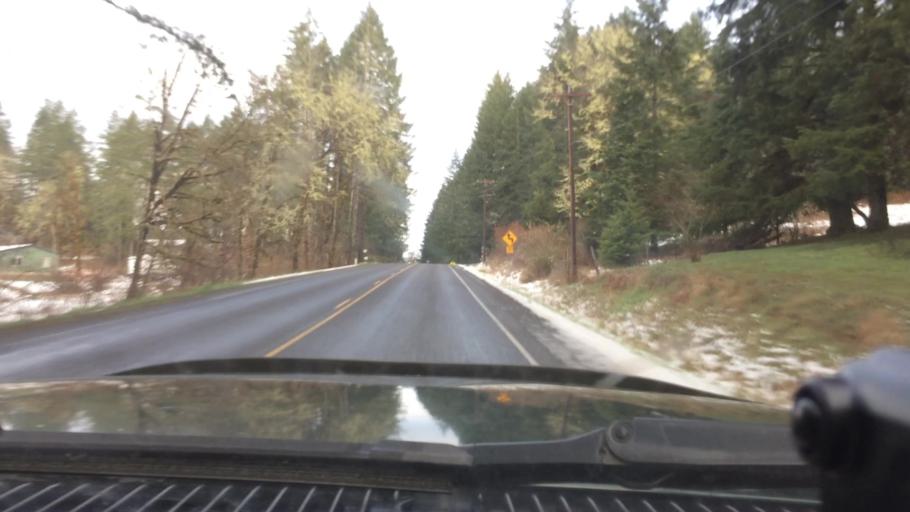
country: US
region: Oregon
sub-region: Lane County
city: Veneta
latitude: 44.1361
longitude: -123.3530
